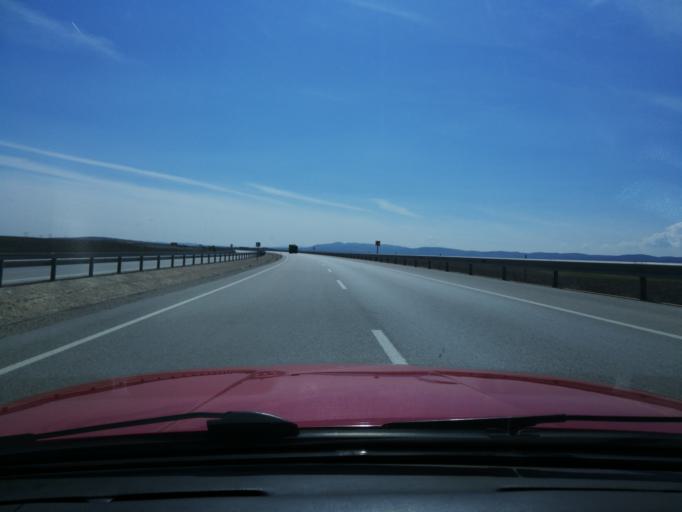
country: TR
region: Kuetahya
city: Altintas
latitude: 39.0352
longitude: 30.2478
